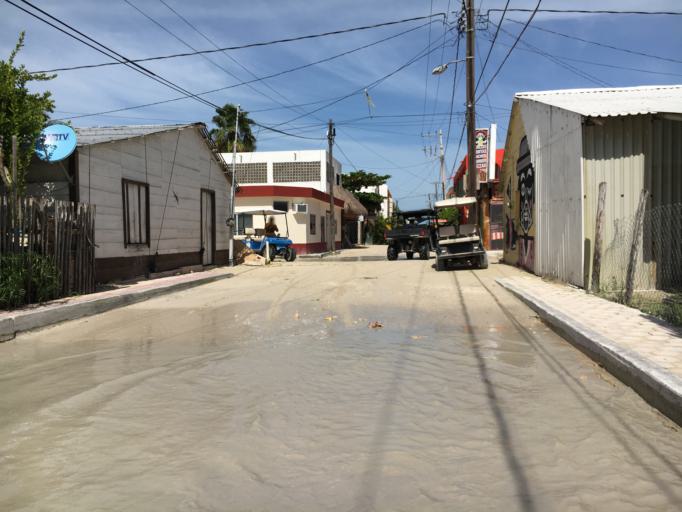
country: MX
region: Quintana Roo
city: Kantunilkin
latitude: 21.5231
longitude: -87.3777
